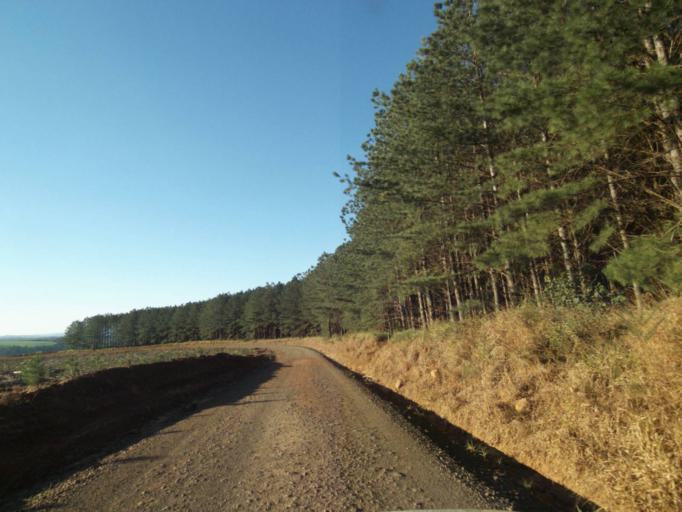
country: BR
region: Parana
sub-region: Telemaco Borba
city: Telemaco Borba
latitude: -24.4488
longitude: -50.5982
